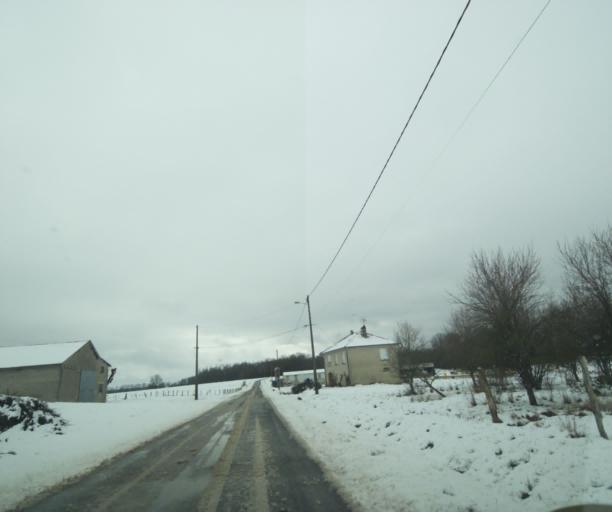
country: FR
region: Champagne-Ardenne
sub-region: Departement de la Haute-Marne
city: Montier-en-Der
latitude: 48.4299
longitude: 4.7281
